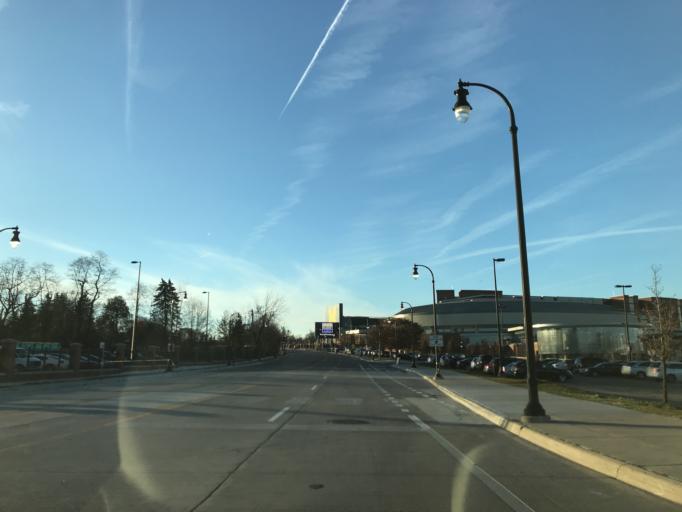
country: US
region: Michigan
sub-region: Washtenaw County
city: Ann Arbor
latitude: 42.2636
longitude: -83.7437
